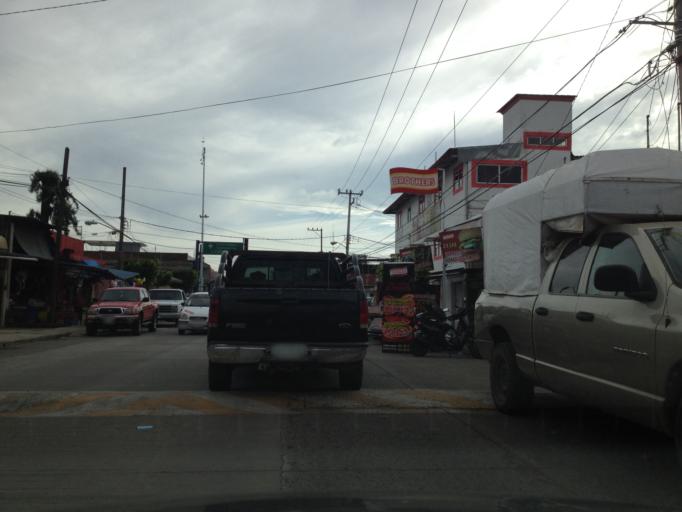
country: MX
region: Michoacan
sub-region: Uruapan
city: Uruapan
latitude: 19.4192
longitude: -102.0368
